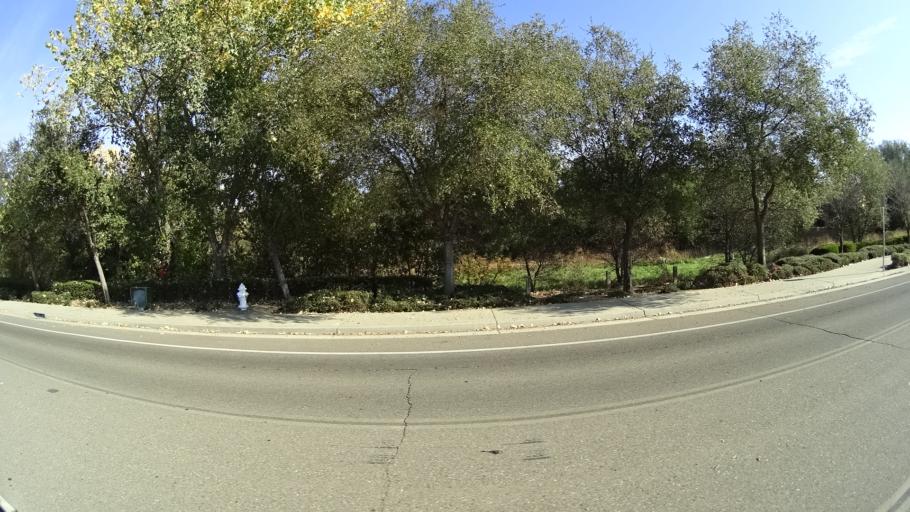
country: US
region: California
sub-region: Sacramento County
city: Citrus Heights
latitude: 38.6837
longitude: -121.2958
